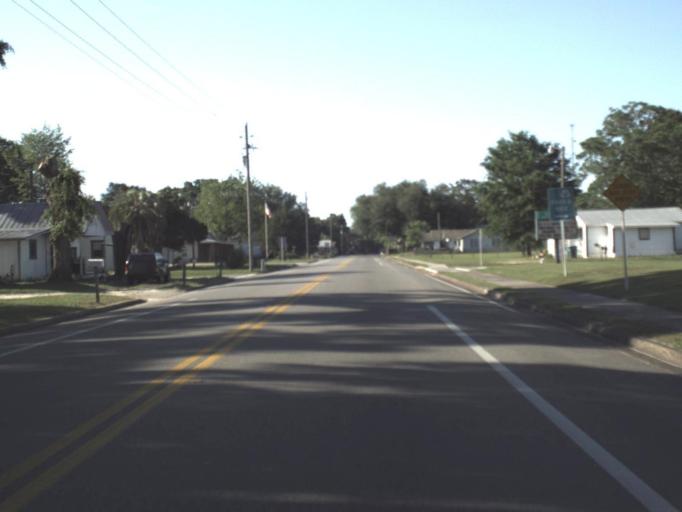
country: US
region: Florida
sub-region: Liberty County
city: Bristol
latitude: 30.3843
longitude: -84.7984
